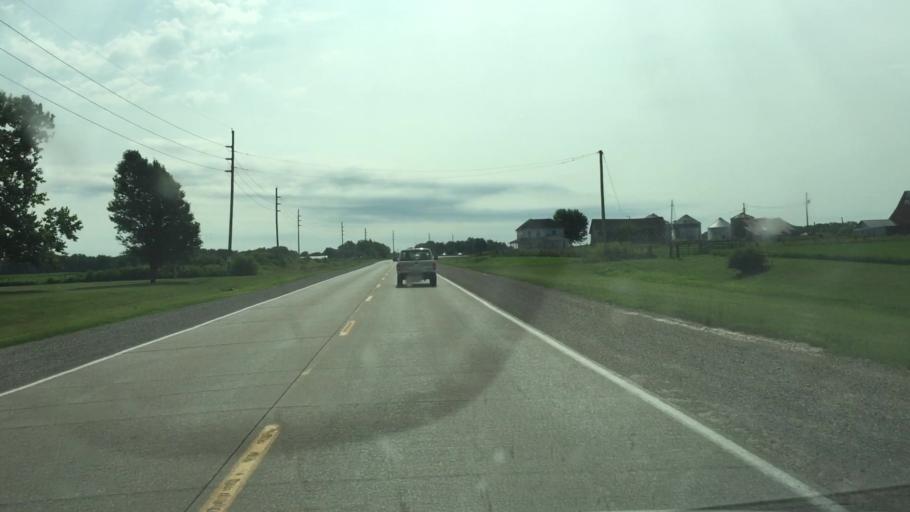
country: US
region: Illinois
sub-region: Hancock County
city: Nauvoo
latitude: 40.6318
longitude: -91.5034
